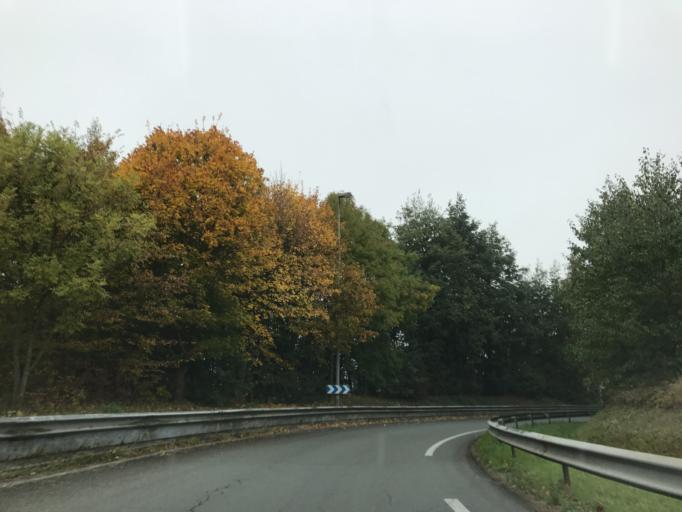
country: FR
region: Nord-Pas-de-Calais
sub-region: Departement du Pas-de-Calais
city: Saint-Laurent-Blangy
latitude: 50.3082
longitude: 2.8015
